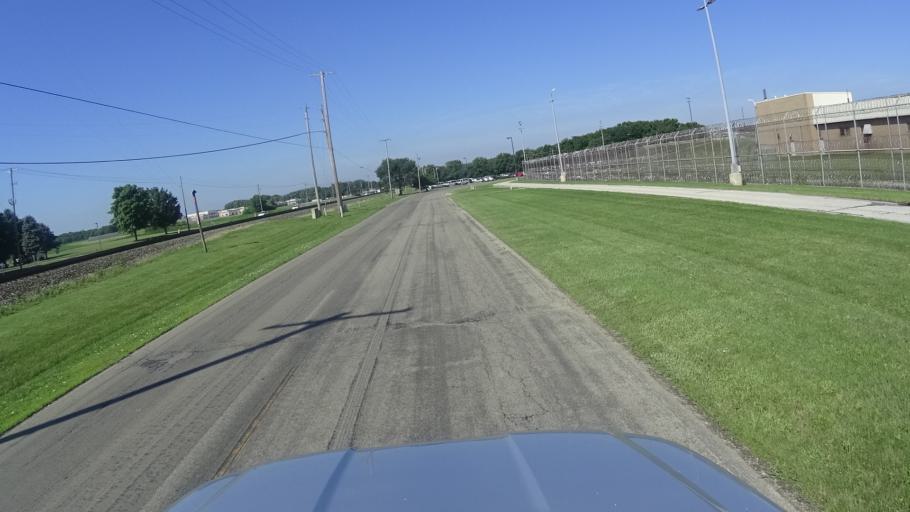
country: US
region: Indiana
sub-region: Madison County
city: Pendleton
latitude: 39.9745
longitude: -85.7701
